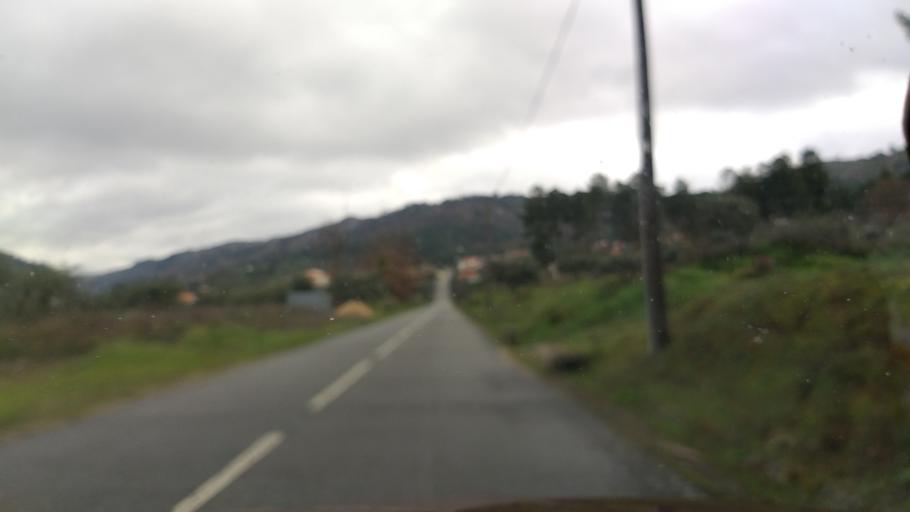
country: PT
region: Guarda
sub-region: Celorico da Beira
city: Celorico da Beira
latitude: 40.7074
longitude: -7.4384
